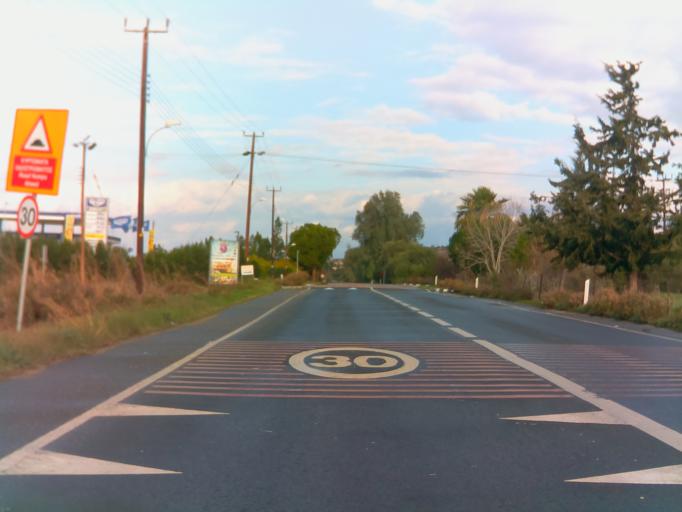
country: CY
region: Pafos
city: Pegeia
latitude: 34.8605
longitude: 32.3736
